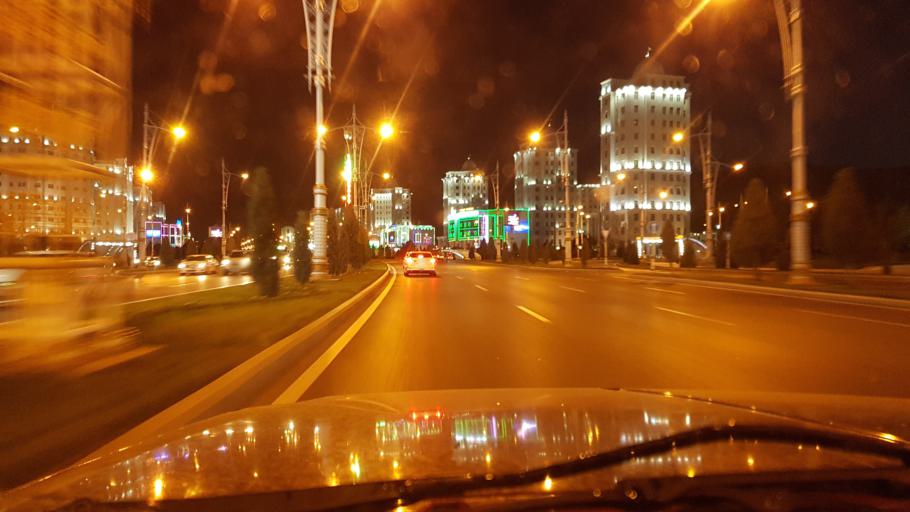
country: TM
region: Ahal
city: Ashgabat
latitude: 37.9066
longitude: 58.3366
